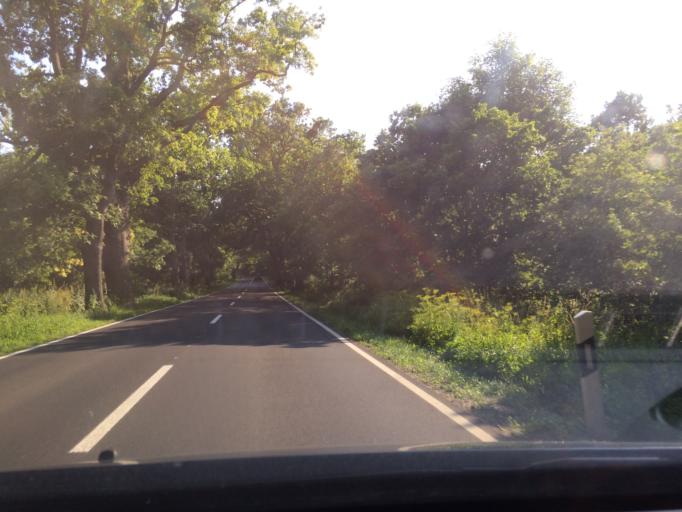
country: DE
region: Mecklenburg-Vorpommern
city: Ostseebad Binz
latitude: 54.4261
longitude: 13.5477
